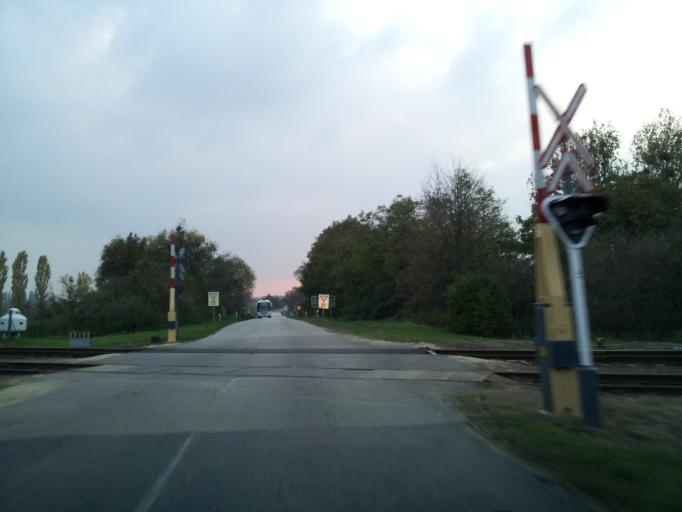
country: HU
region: Gyor-Moson-Sopron
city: Bakonyszentlaszlo
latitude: 47.4478
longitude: 17.8169
